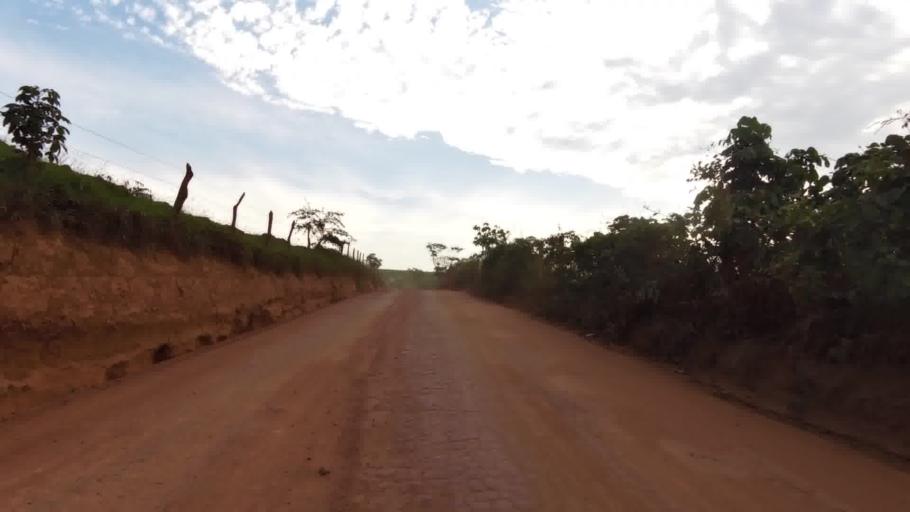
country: BR
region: Espirito Santo
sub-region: Piuma
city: Piuma
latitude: -20.8343
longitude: -40.7420
